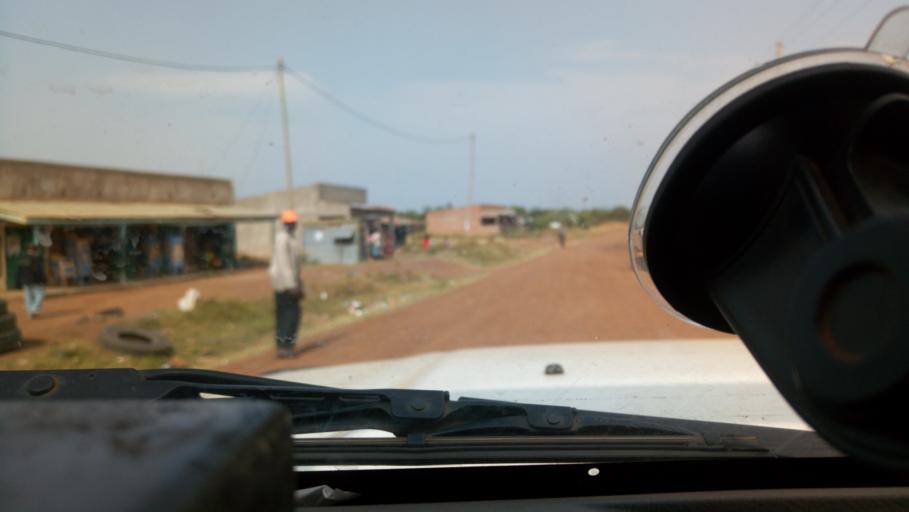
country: KE
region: Migori
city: Migori
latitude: -0.9319
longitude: 34.2229
